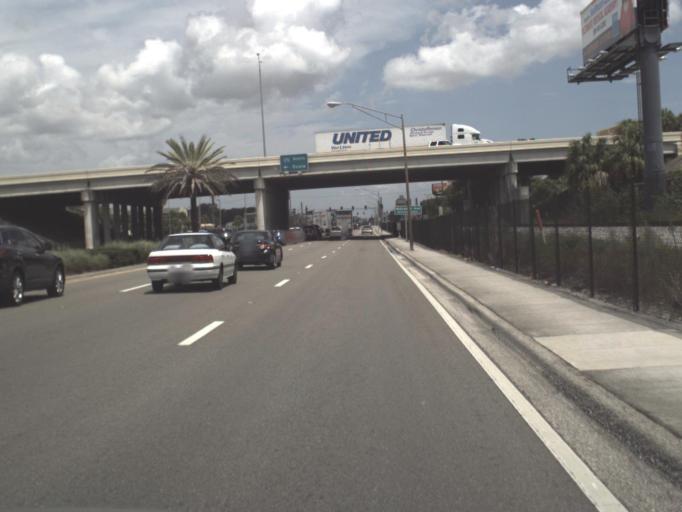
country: US
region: Florida
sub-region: Hillsborough County
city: Carrollwood
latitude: 28.0328
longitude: -82.4563
